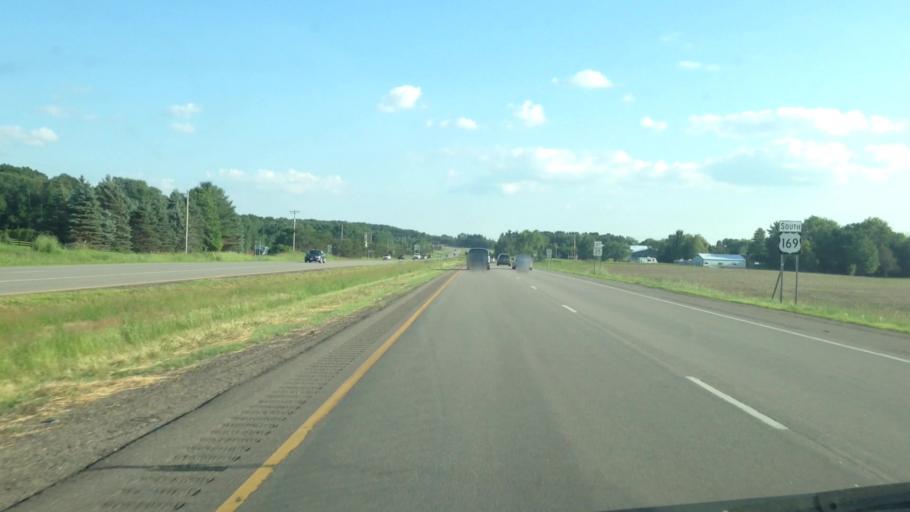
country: US
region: Minnesota
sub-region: Sherburne County
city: Zimmerman
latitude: 45.4147
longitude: -93.5658
